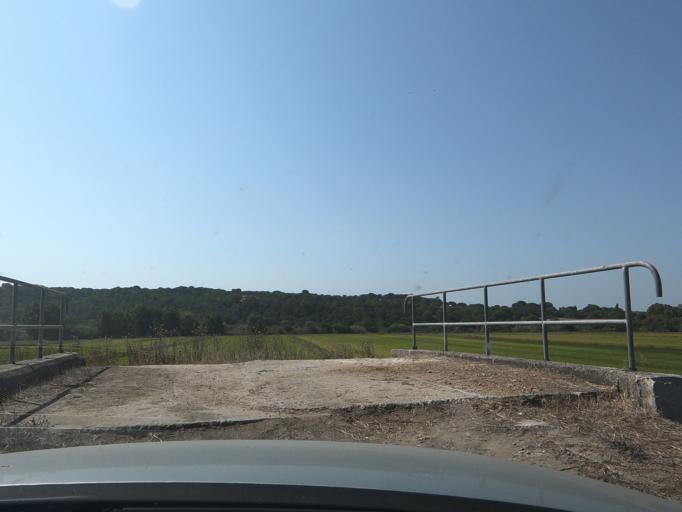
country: PT
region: Setubal
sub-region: Alcacer do Sal
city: Alcacer do Sal
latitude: 38.2857
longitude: -8.4029
